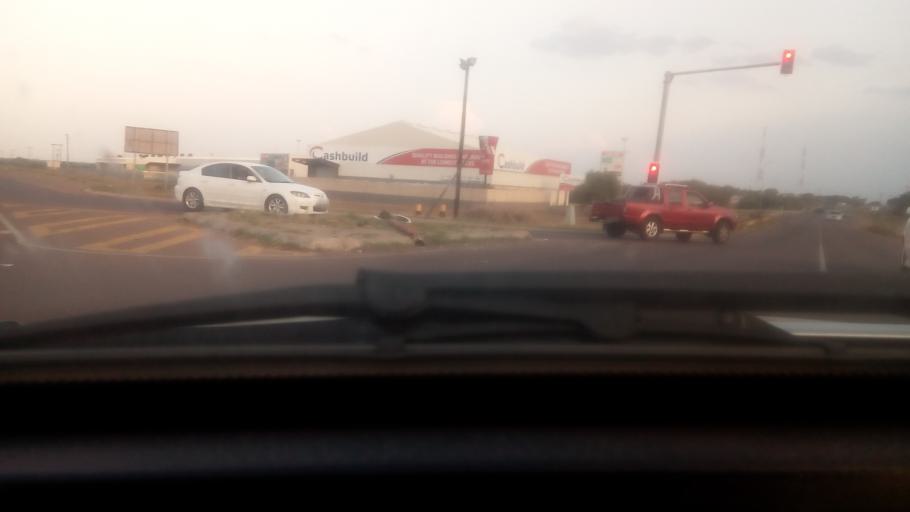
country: BW
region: Kgatleng
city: Mochudi
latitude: -24.4000
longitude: 26.0787
